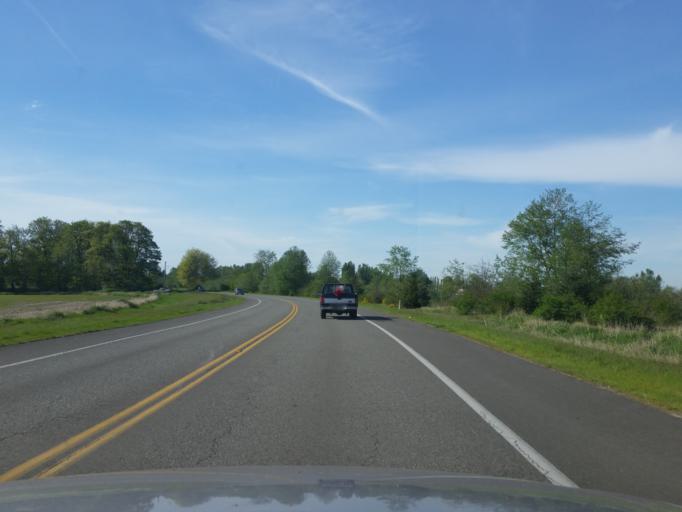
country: US
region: Washington
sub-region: Snohomish County
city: Everett
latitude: 47.9402
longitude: -122.1720
